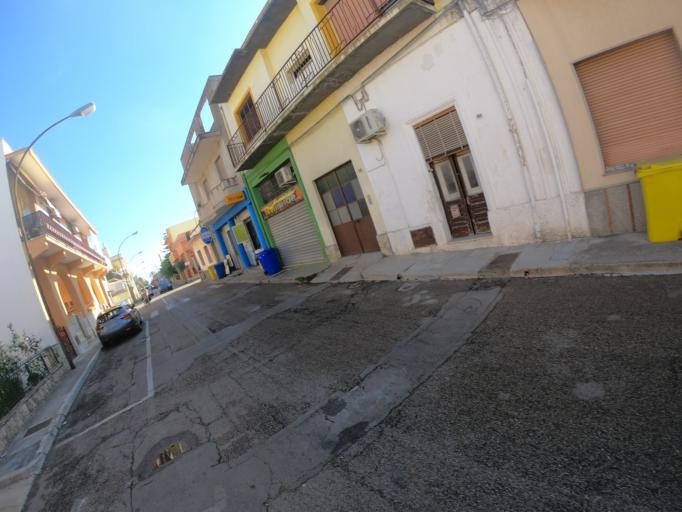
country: IT
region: Apulia
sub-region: Provincia di Lecce
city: Supersano
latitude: 40.0144
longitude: 18.2413
